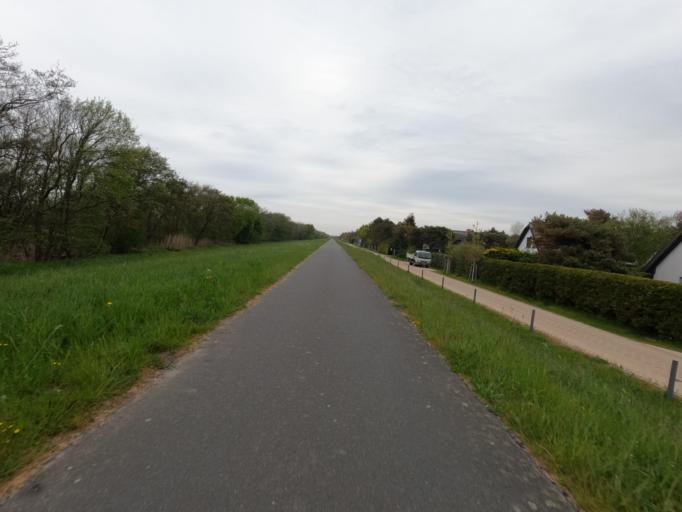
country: DE
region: Mecklenburg-Vorpommern
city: Ostseebad Dierhagen
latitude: 54.3256
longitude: 12.3677
